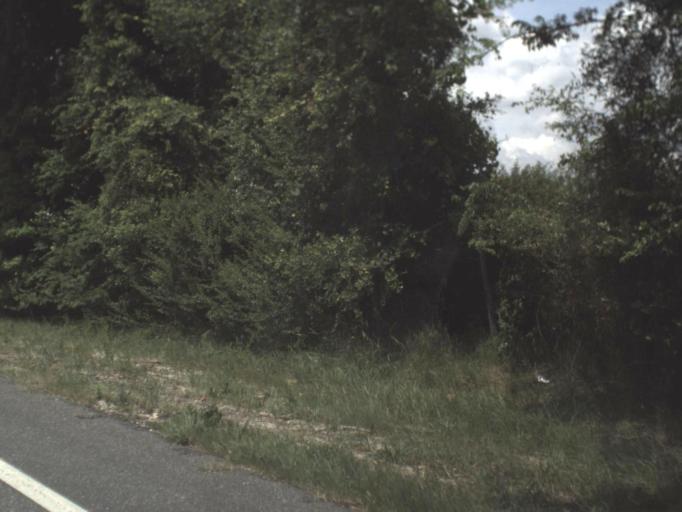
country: US
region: Florida
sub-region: Alachua County
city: Newberry
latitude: 29.6270
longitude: -82.6018
